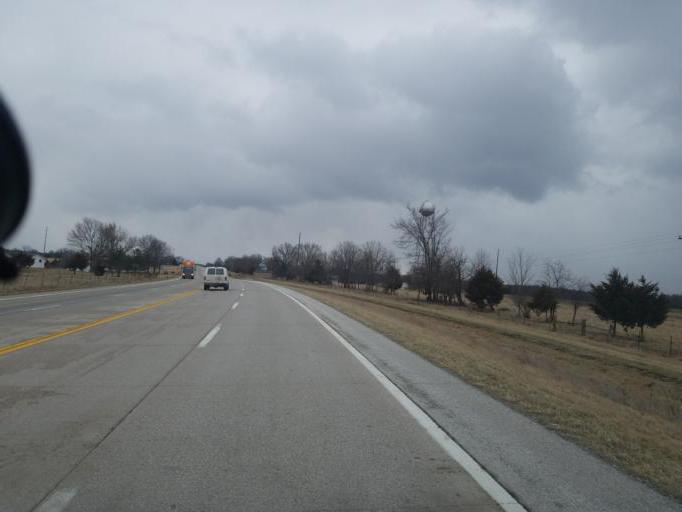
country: US
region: Missouri
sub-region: Macon County
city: Macon
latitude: 39.7831
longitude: -92.4812
